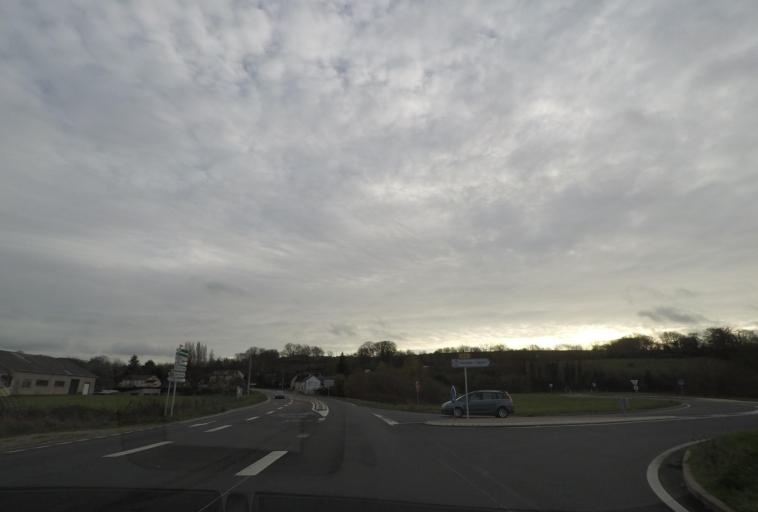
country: FR
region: Centre
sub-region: Departement du Loir-et-Cher
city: Sarge-sur-Braye
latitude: 47.9101
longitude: 0.8454
